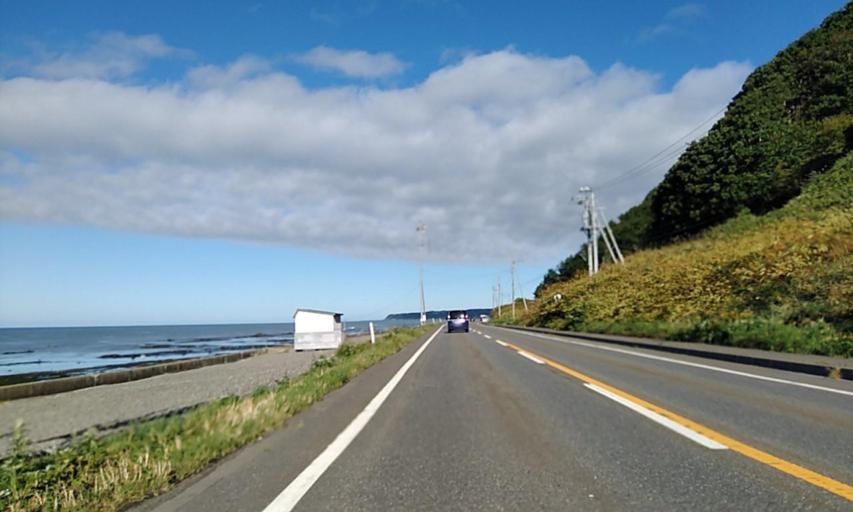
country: JP
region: Hokkaido
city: Shizunai-furukawacho
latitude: 42.2816
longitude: 142.4689
